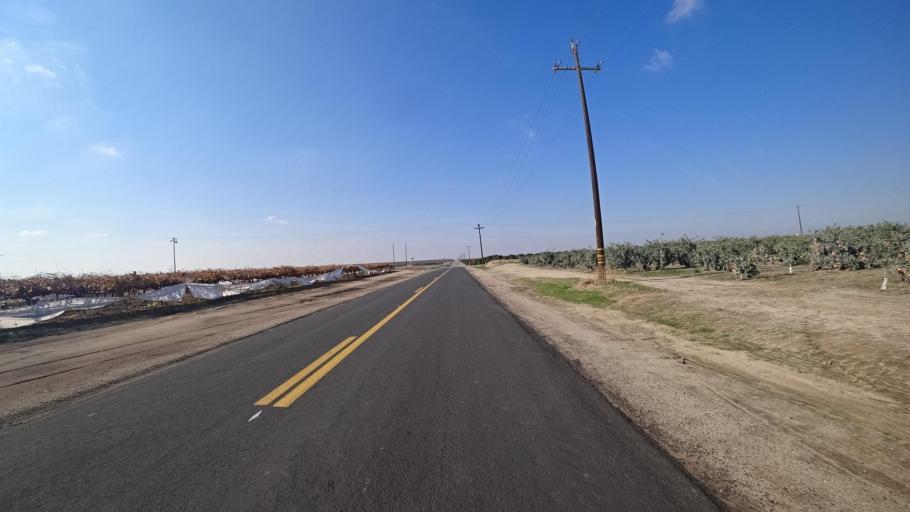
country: US
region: California
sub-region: Kern County
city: Arvin
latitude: 35.2675
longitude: -118.7876
